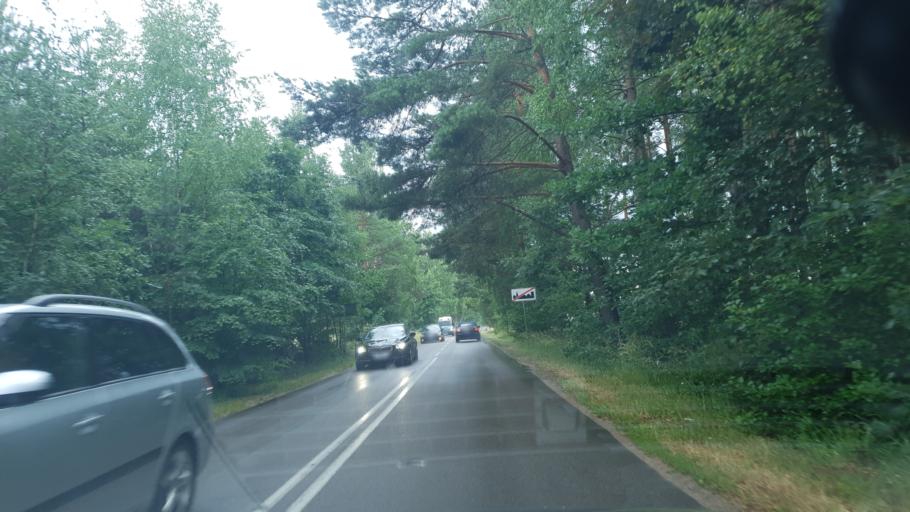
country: PL
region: Pomeranian Voivodeship
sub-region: Powiat kartuski
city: Stezyca
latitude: 54.2457
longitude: 17.9996
